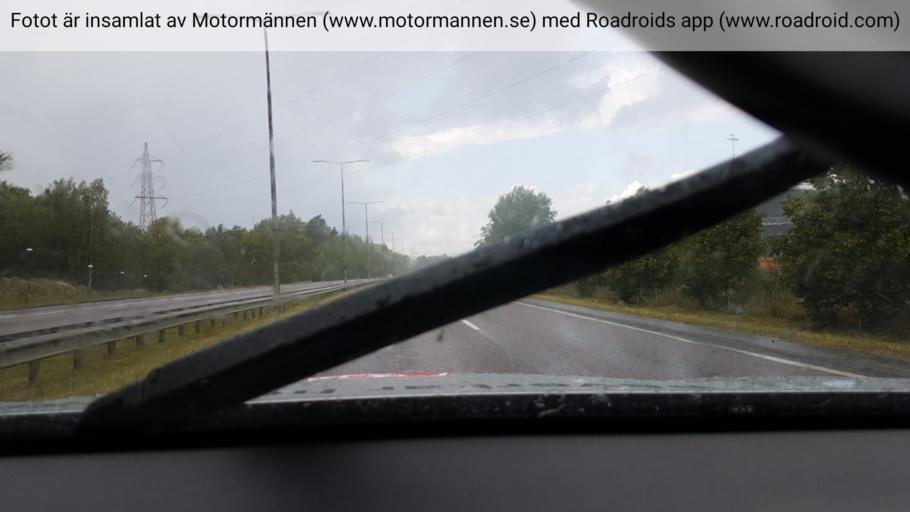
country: SE
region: Stockholm
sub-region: Stockholms Kommun
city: Arsta
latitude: 59.2596
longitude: 18.0726
